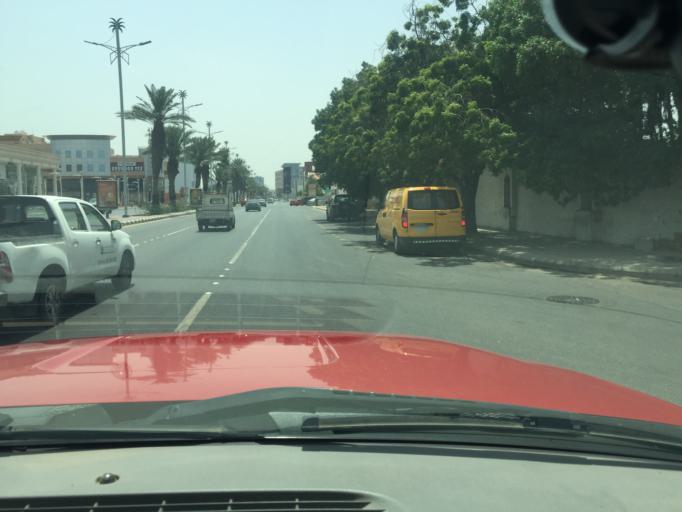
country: SA
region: Makkah
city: Jeddah
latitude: 21.5485
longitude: 39.1445
